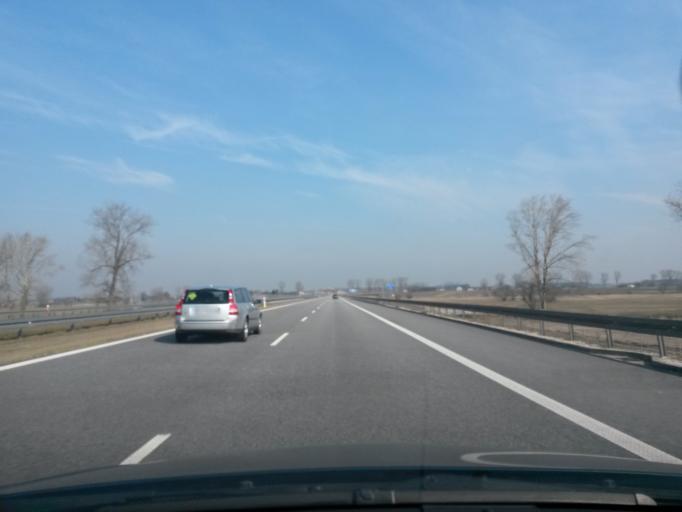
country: PL
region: Lodz Voivodeship
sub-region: Powiat kutnowski
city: Krzyzanow
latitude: 52.1725
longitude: 19.4855
